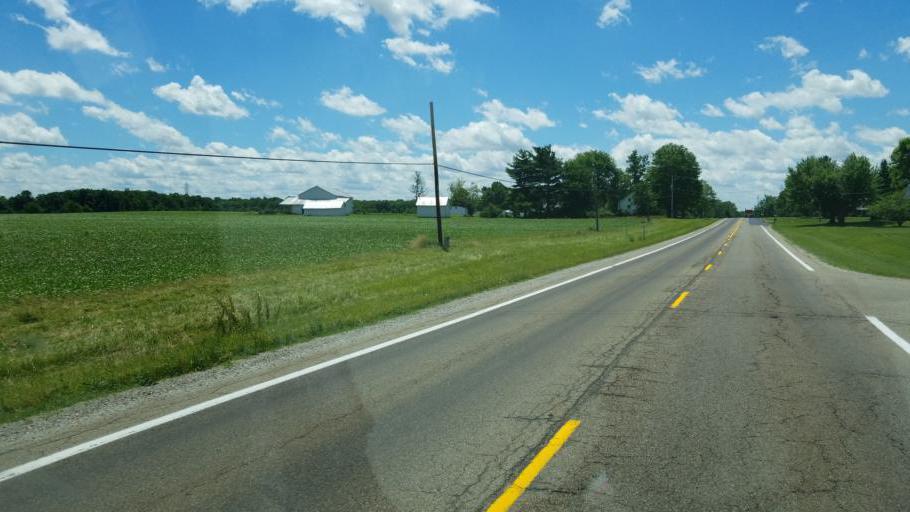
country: US
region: Ohio
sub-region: Crawford County
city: Galion
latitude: 40.6972
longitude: -82.8181
